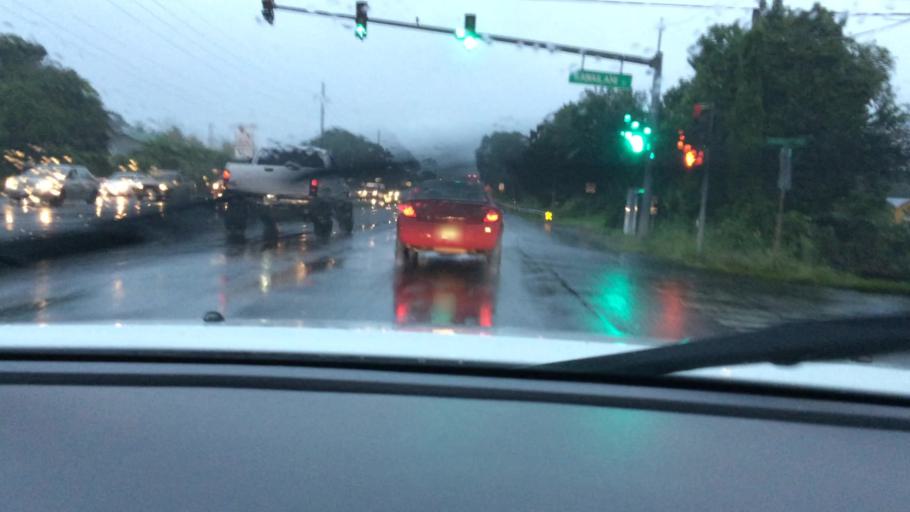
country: US
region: Hawaii
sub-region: Hawaii County
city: Hilo
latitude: 19.6848
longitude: -155.0654
